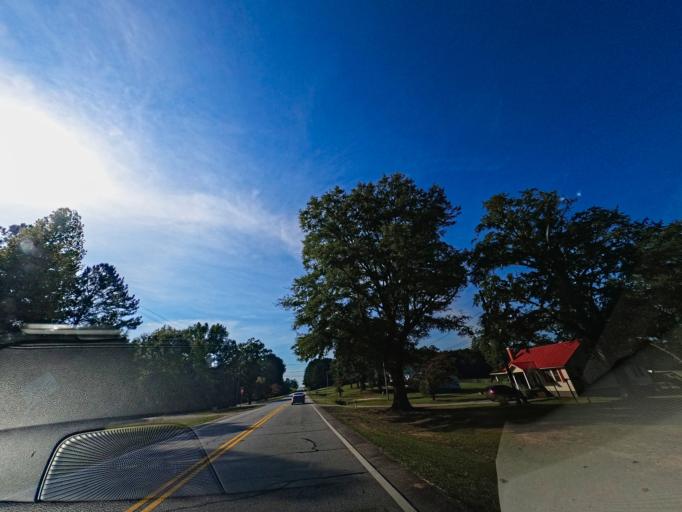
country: US
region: Georgia
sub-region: Troup County
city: Hogansville
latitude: 33.2102
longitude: -84.9226
